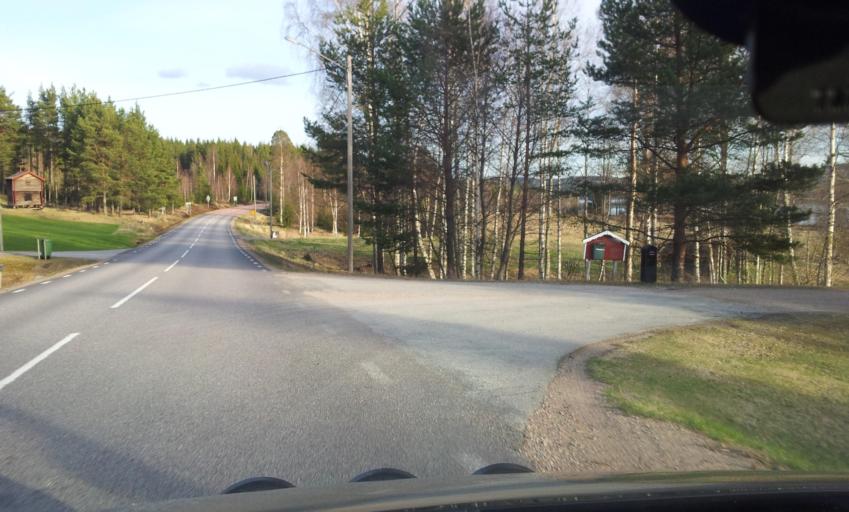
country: SE
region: Vaesternorrland
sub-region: Ange Kommun
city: Ange
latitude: 62.1541
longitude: 15.6781
